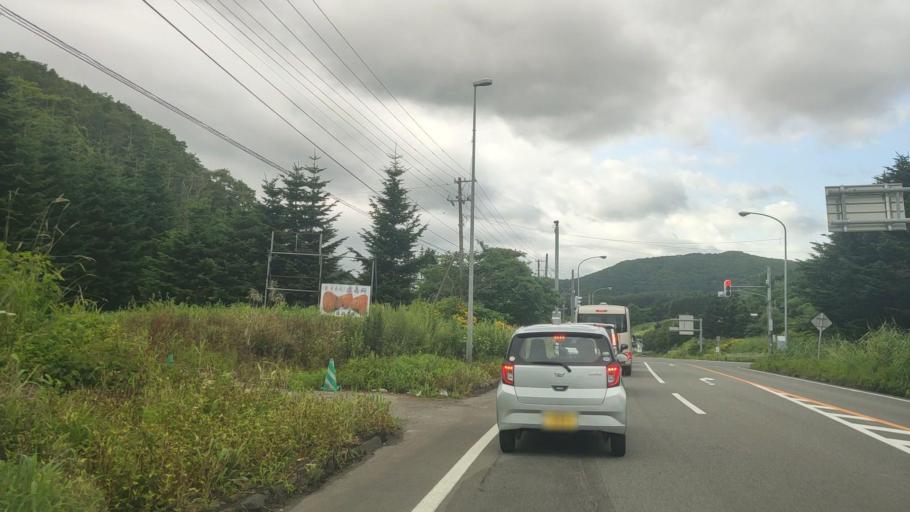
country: JP
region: Hokkaido
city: Date
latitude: 42.5760
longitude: 140.7239
